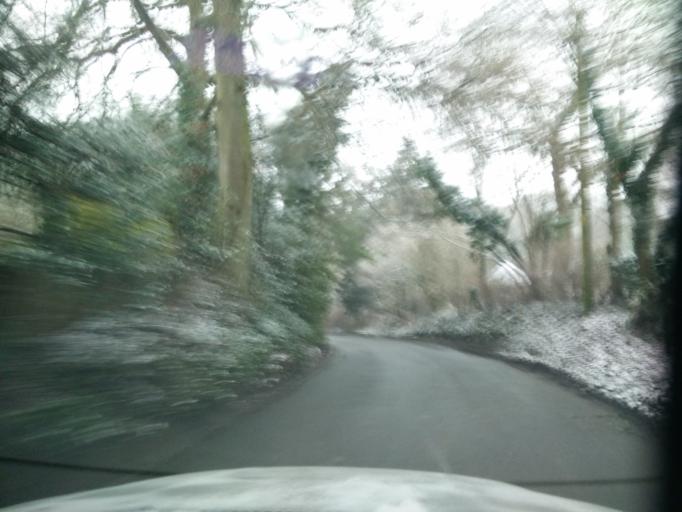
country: GB
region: England
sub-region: Buckinghamshire
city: Princes Risborough
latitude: 51.7341
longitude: -0.8052
